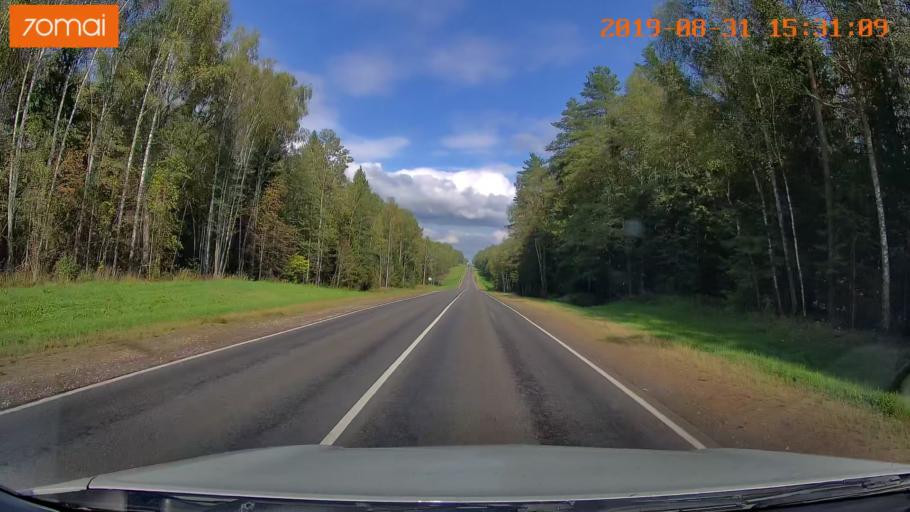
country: RU
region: Kaluga
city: Baryatino
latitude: 54.5805
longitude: 34.6477
